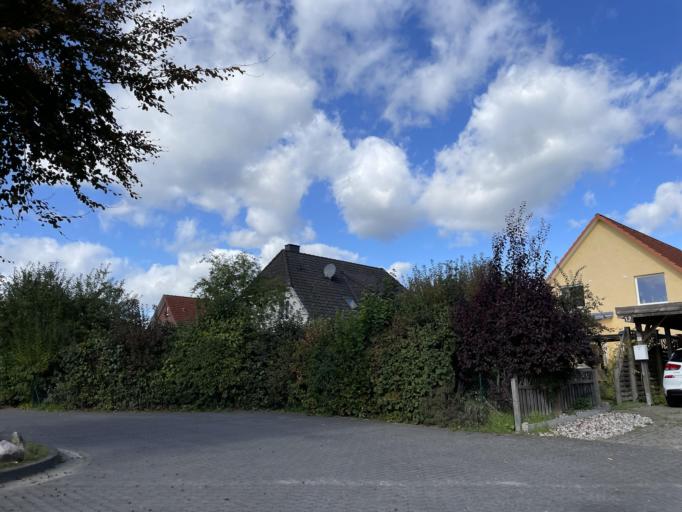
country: DE
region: Lower Saxony
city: Barendorf
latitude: 53.2318
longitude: 10.5179
